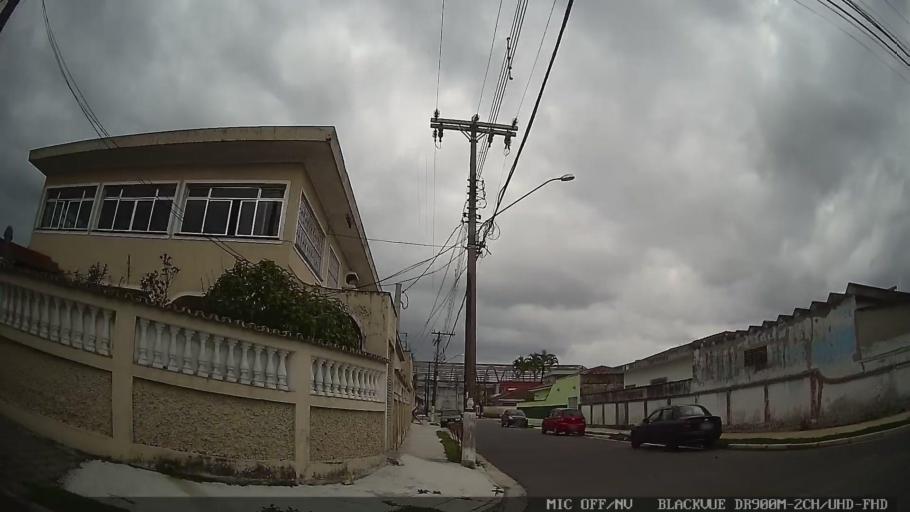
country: BR
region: Sao Paulo
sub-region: Guaruja
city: Guaruja
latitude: -23.9934
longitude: -46.2896
